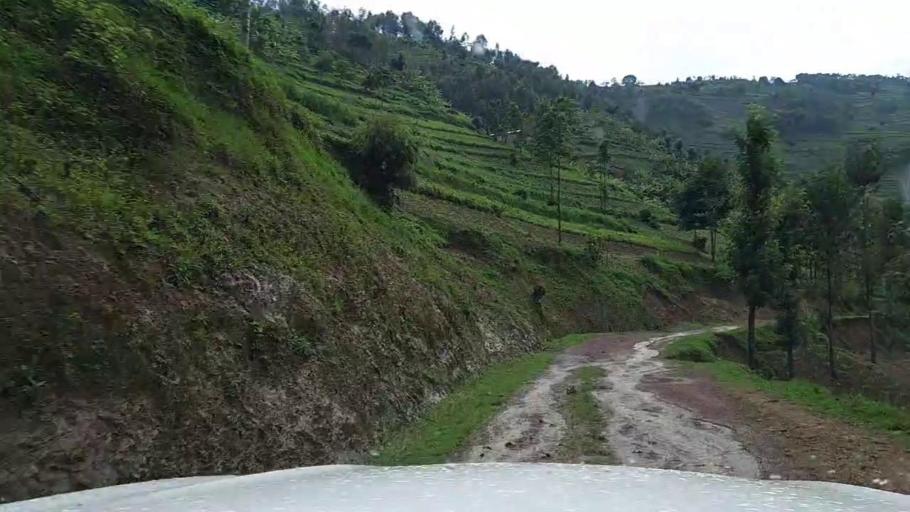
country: RW
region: Northern Province
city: Byumba
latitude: -1.7216
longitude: 29.9129
